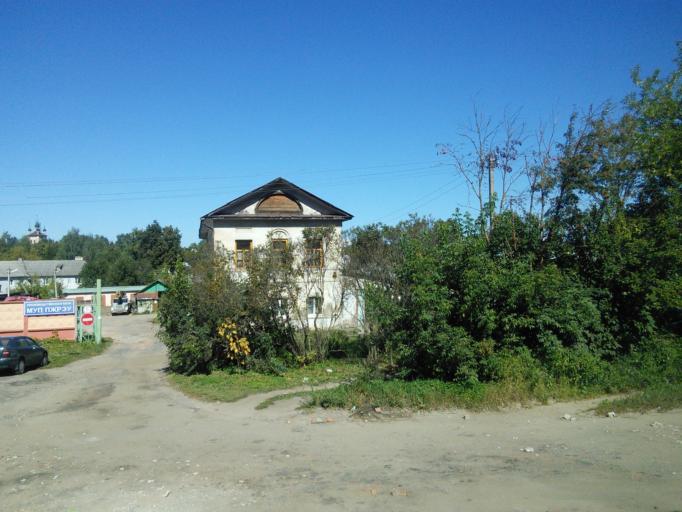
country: RU
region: Tverskaya
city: Kashin
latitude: 57.3633
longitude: 37.6120
